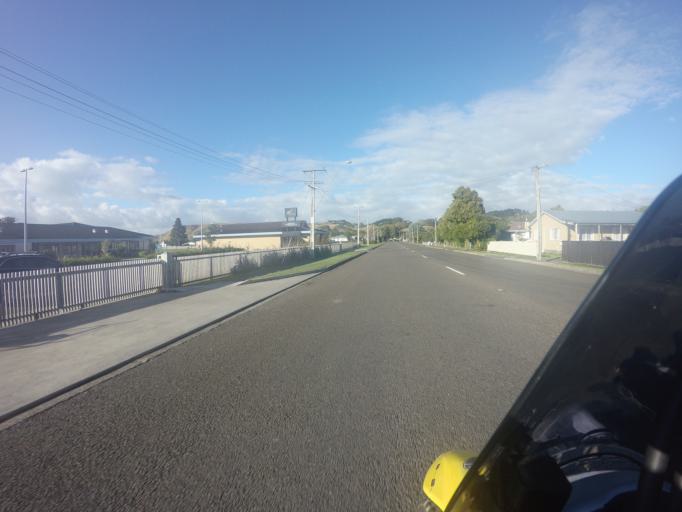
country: NZ
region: Gisborne
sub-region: Gisborne District
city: Gisborne
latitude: -38.6742
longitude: 178.0501
